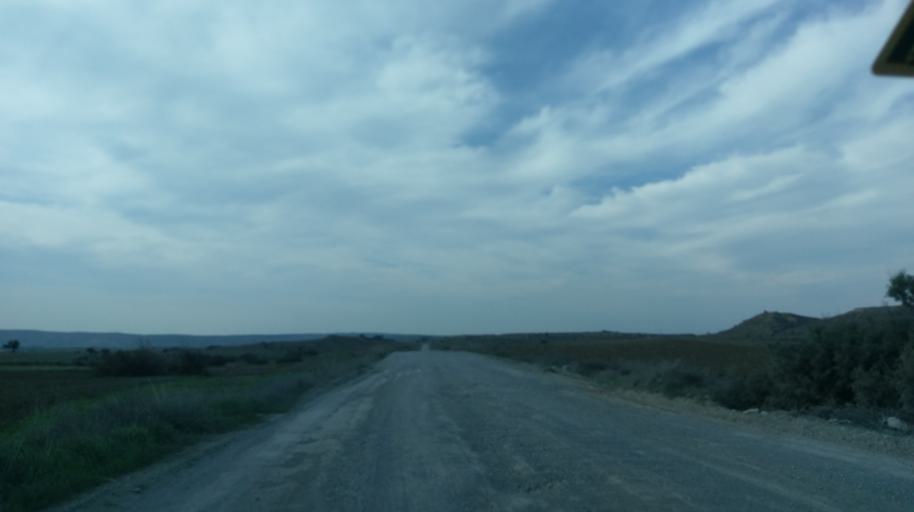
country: CY
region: Keryneia
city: Lapithos
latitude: 35.2864
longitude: 33.1468
